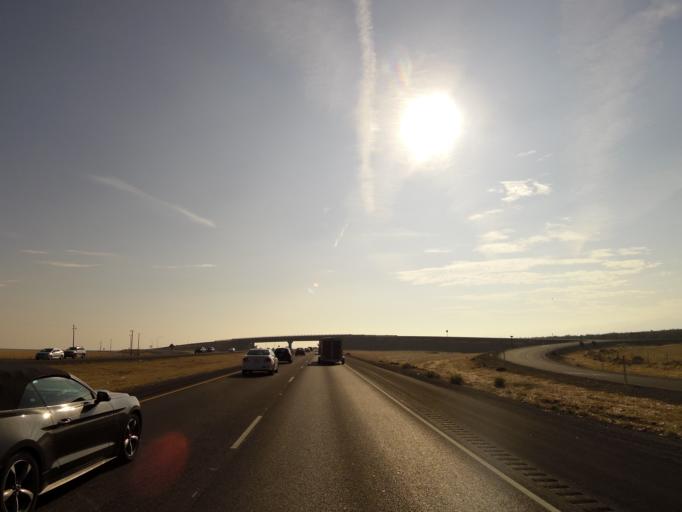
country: US
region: California
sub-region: Fresno County
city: Mendota
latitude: 36.6064
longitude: -120.5883
